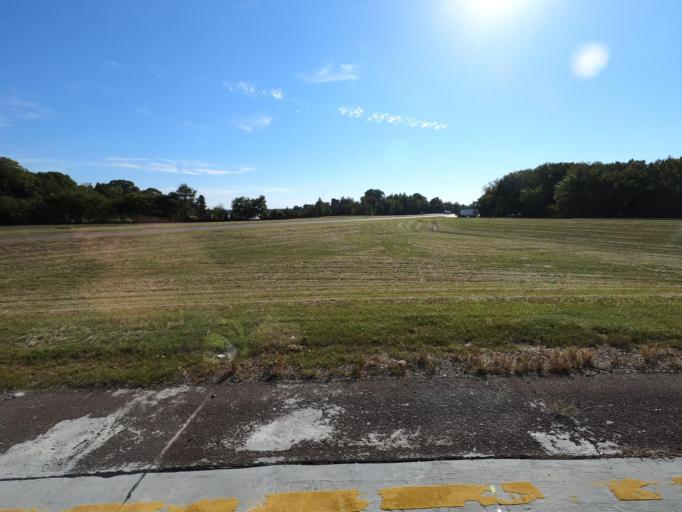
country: US
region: Tennessee
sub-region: Dyer County
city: Dyersburg
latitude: 36.0724
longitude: -89.3497
